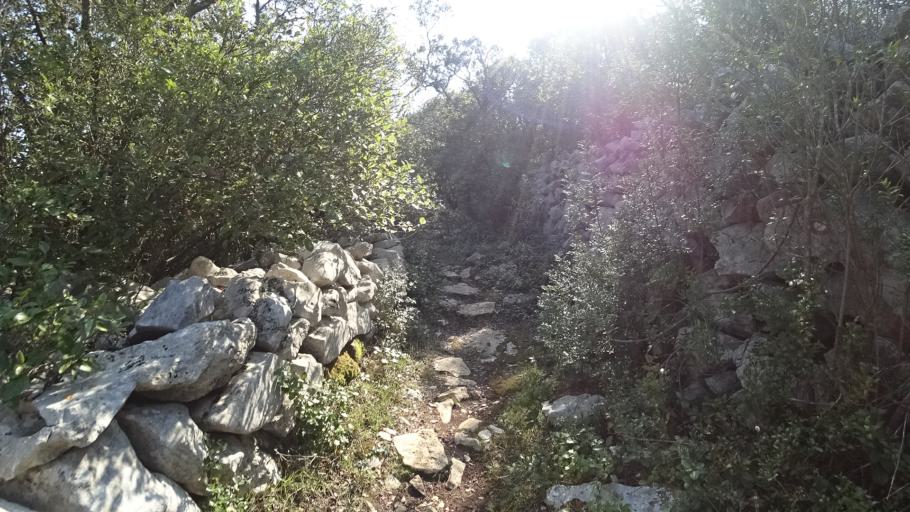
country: HR
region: Primorsko-Goranska
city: Mali Losinj
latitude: 44.4972
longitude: 14.5249
